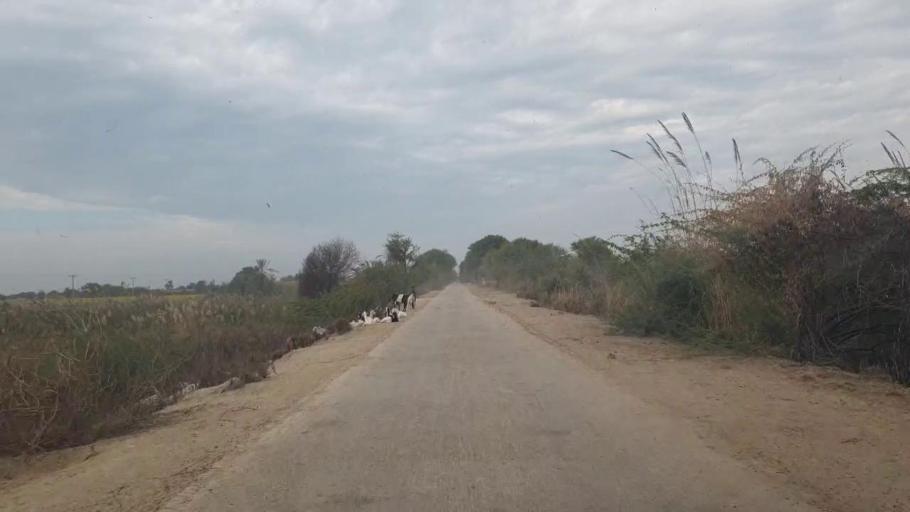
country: PK
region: Sindh
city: Jhol
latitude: 25.9934
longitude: 68.8927
